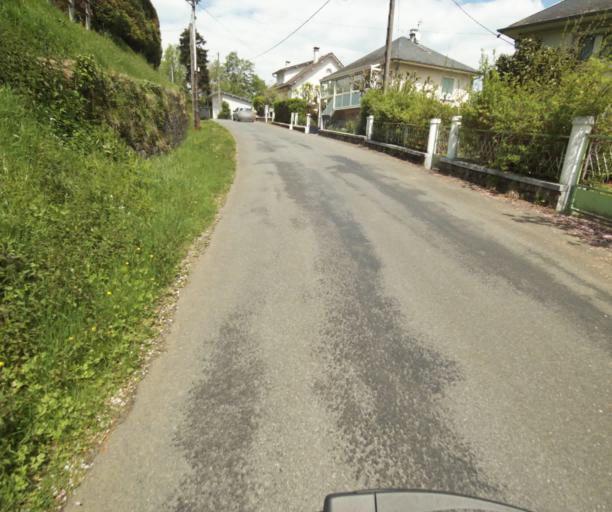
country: FR
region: Limousin
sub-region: Departement de la Correze
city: Tulle
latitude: 45.2764
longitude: 1.7582
